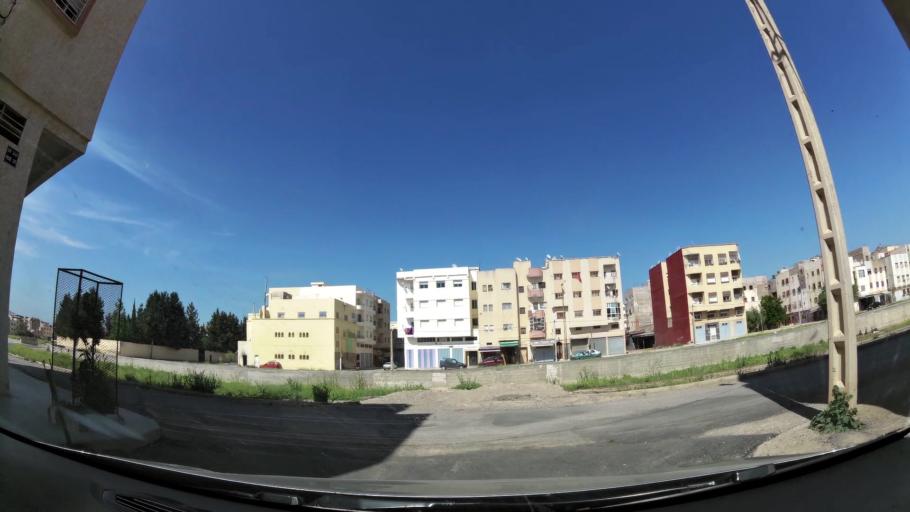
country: MA
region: Fes-Boulemane
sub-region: Fes
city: Fes
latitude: 34.0098
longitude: -5.0332
